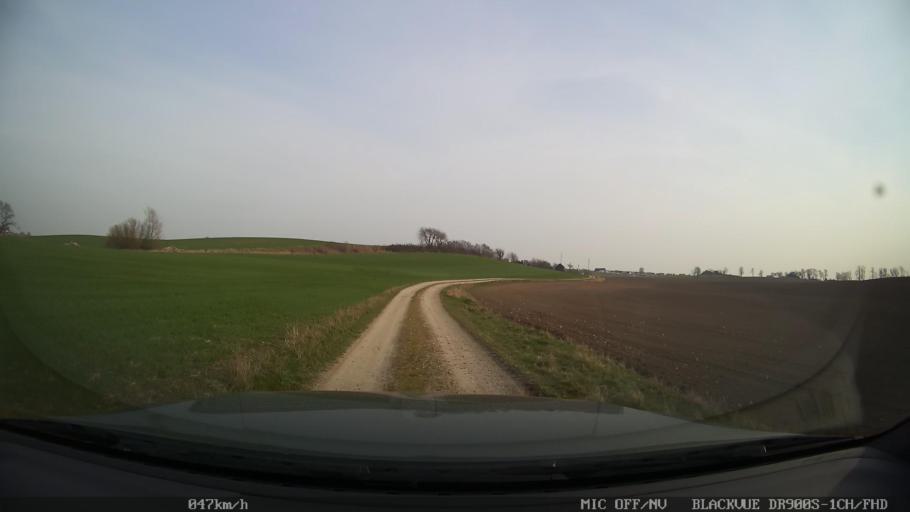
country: SE
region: Skane
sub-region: Ystads Kommun
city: Ystad
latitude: 55.4550
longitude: 13.7920
